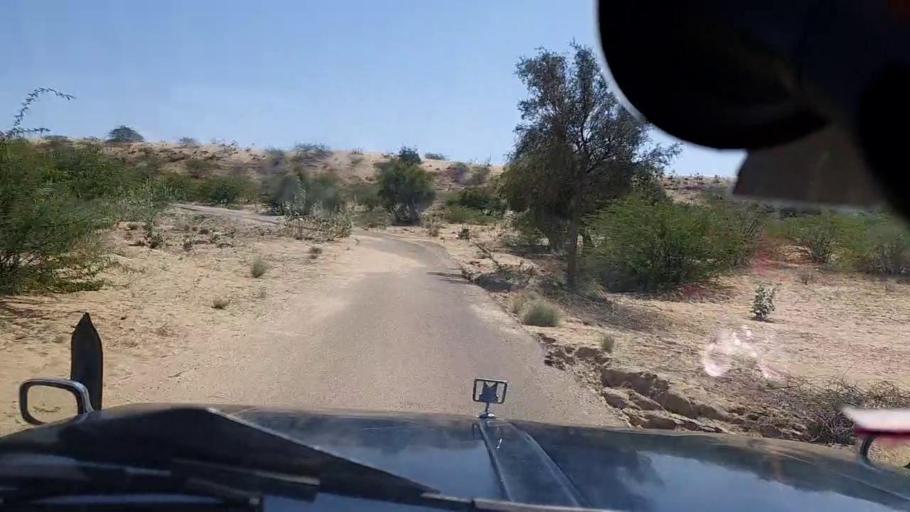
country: PK
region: Sindh
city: Diplo
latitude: 24.5618
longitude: 69.6739
